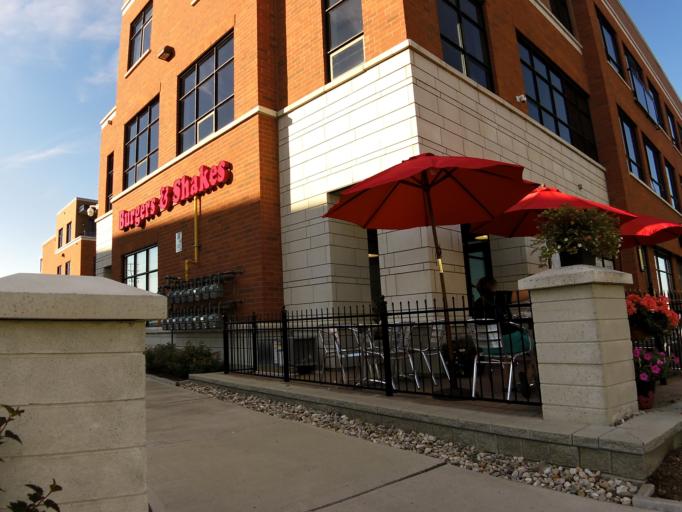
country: CA
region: Ontario
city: Bells Corners
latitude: 45.2648
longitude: -75.7770
